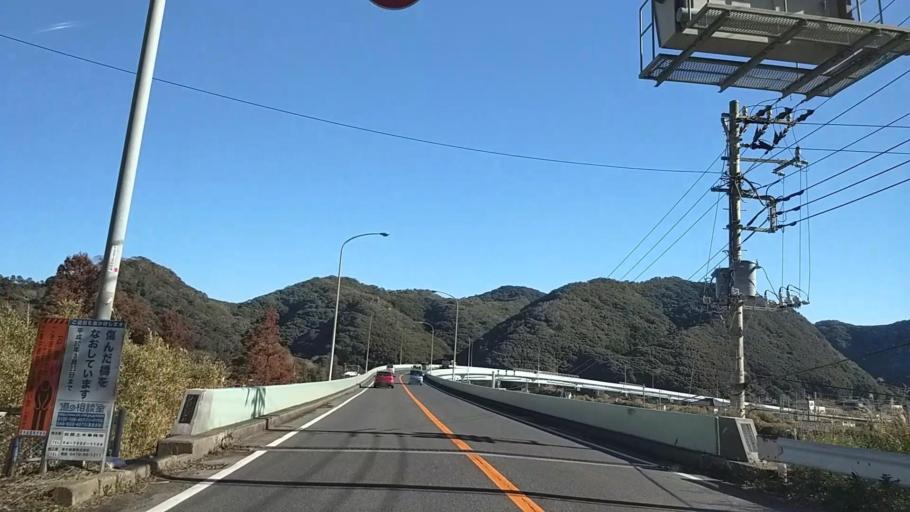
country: JP
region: Chiba
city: Kawaguchi
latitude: 35.1277
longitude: 140.1675
